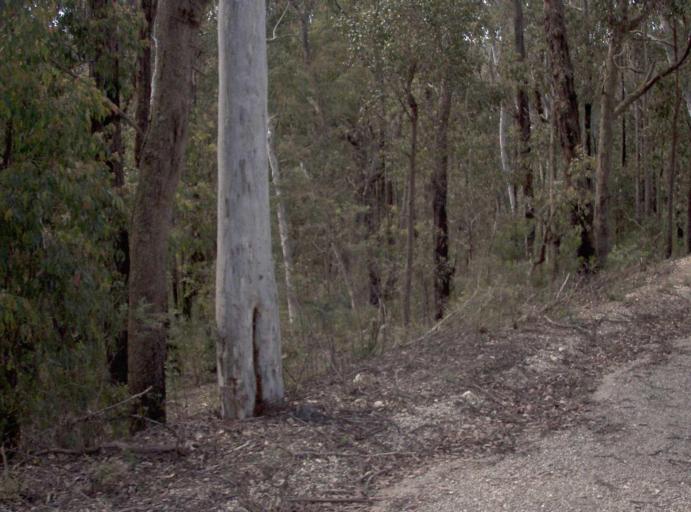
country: AU
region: New South Wales
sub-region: Bombala
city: Bombala
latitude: -37.1833
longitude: 148.7089
